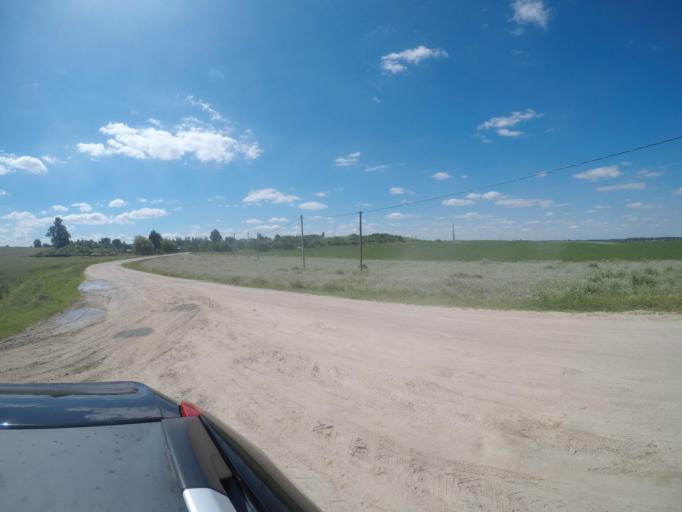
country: BY
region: Grodnenskaya
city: Hrodna
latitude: 53.7306
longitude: 23.8511
